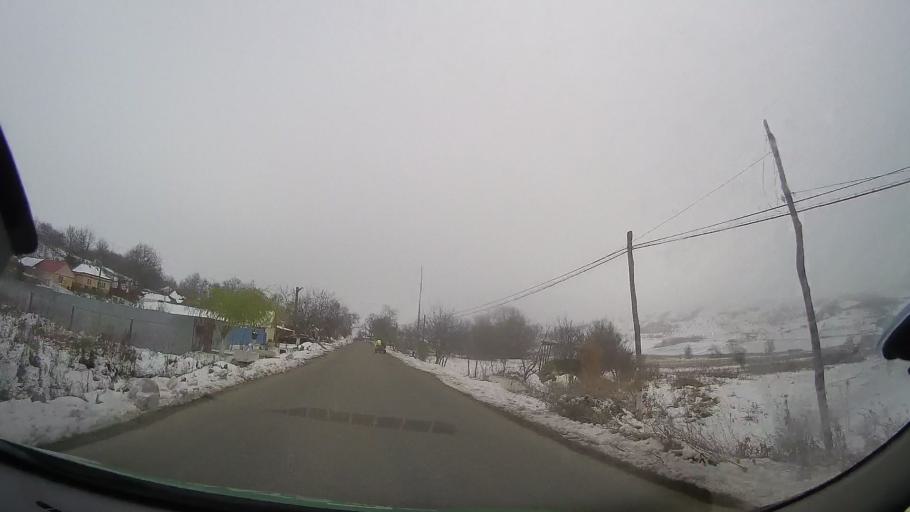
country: RO
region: Bacau
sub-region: Comuna Glavanesti
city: Frumuselu
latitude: 46.2903
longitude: 27.3009
